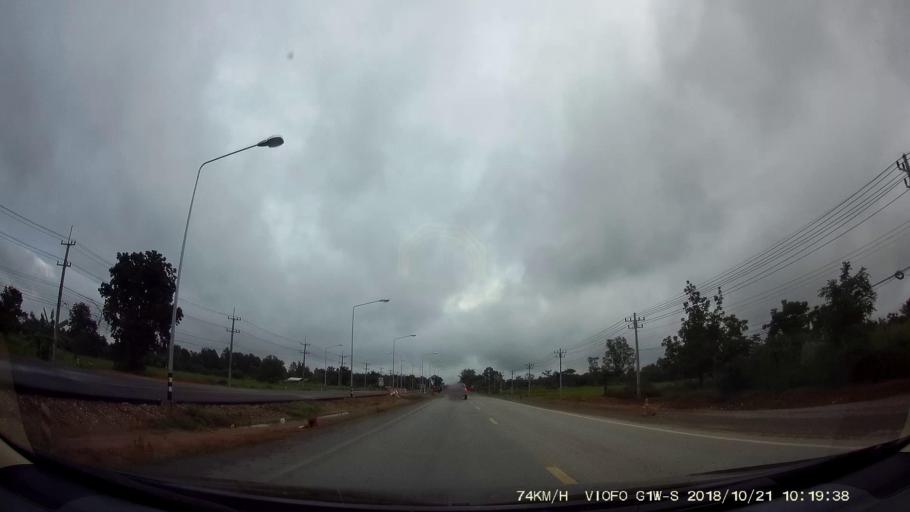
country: TH
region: Chaiyaphum
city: Phu Khiao
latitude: 16.3128
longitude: 102.2000
